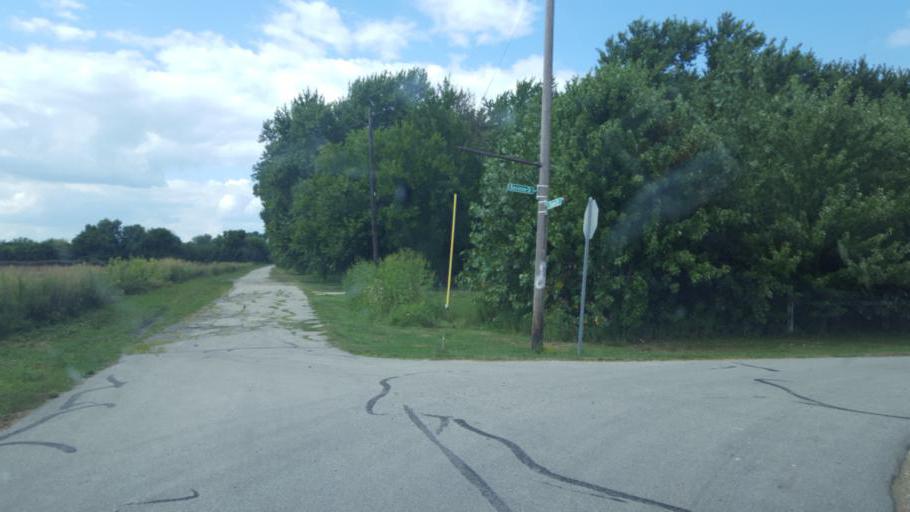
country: US
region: Ohio
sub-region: Lucas County
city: Curtice
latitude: 41.6552
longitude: -83.2508
